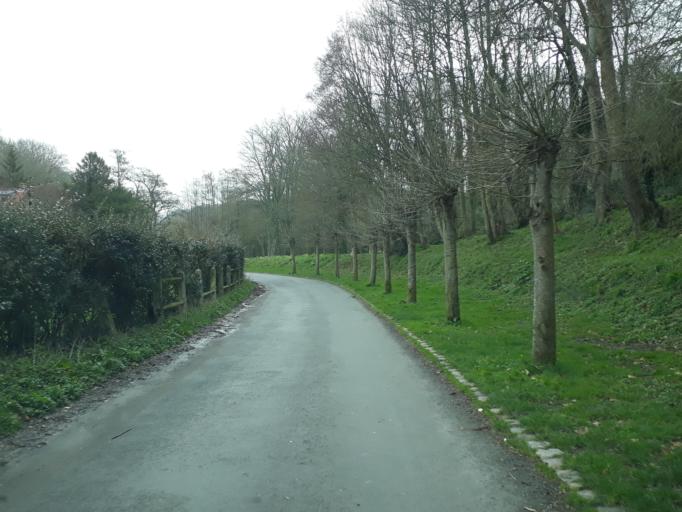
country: FR
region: Haute-Normandie
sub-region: Departement de la Seine-Maritime
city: Yport
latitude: 49.7341
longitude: 0.2909
